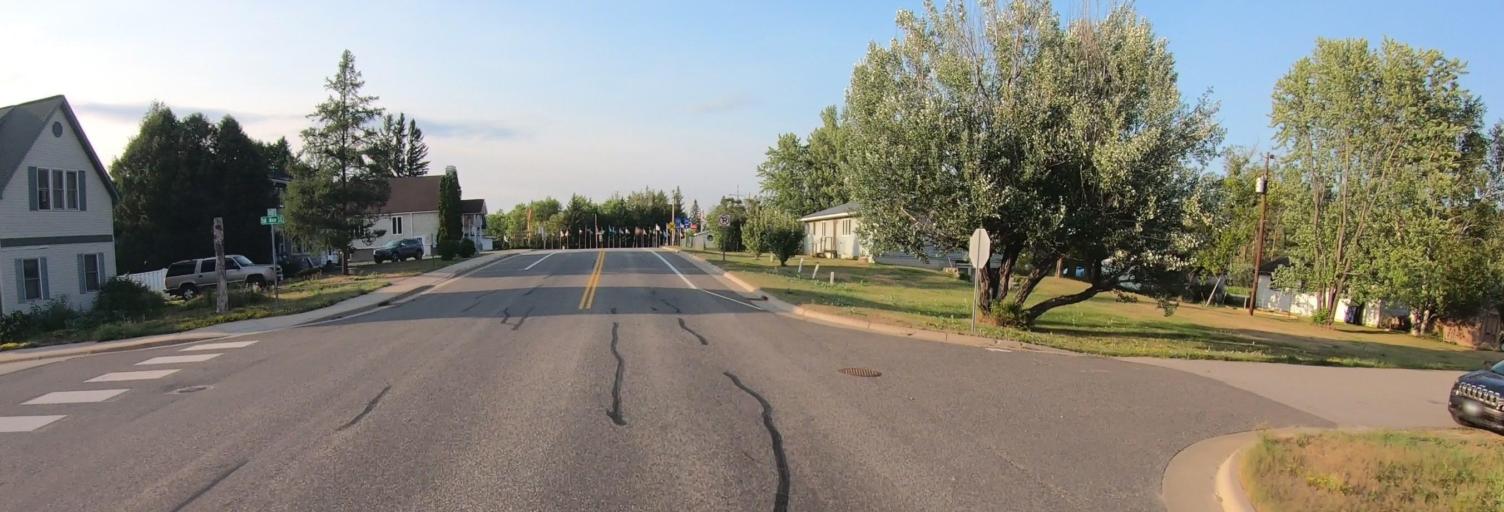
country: US
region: Minnesota
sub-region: Saint Louis County
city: Mountain Iron
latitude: 47.8518
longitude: -92.6822
